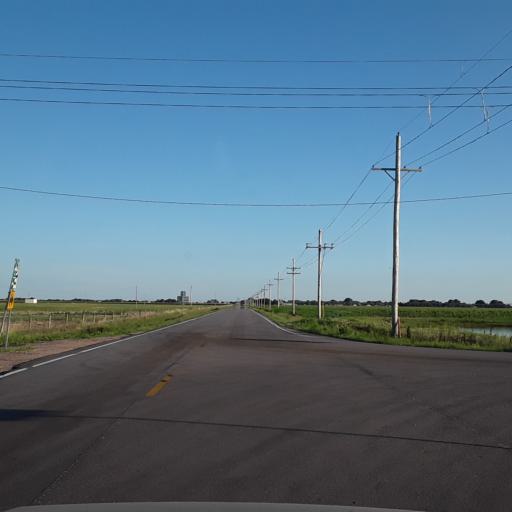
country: US
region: Nebraska
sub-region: Hall County
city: Grand Island
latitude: 40.9601
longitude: -98.3207
